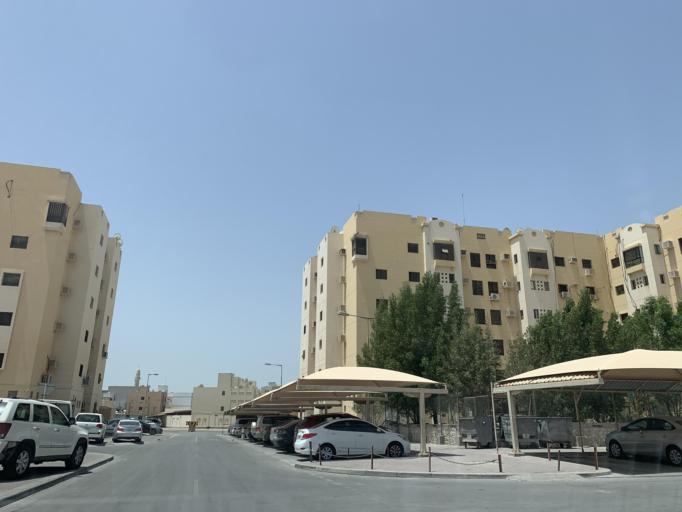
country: BH
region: Northern
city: Sitrah
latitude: 26.1425
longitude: 50.5958
